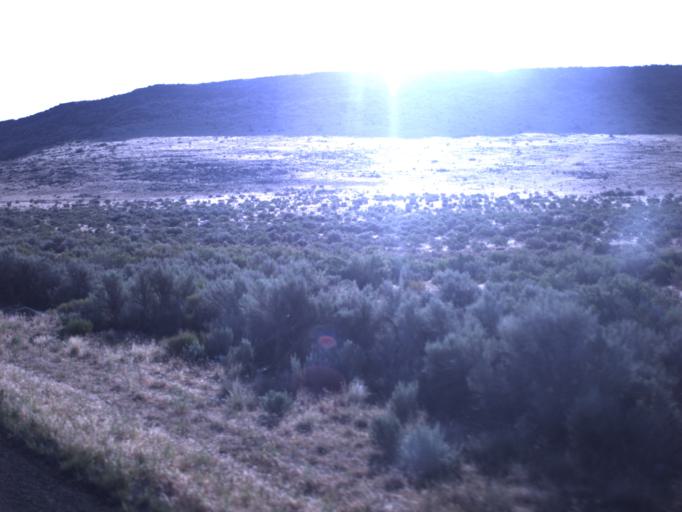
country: US
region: Utah
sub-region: Iron County
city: Enoch
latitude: 37.8467
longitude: -113.0392
